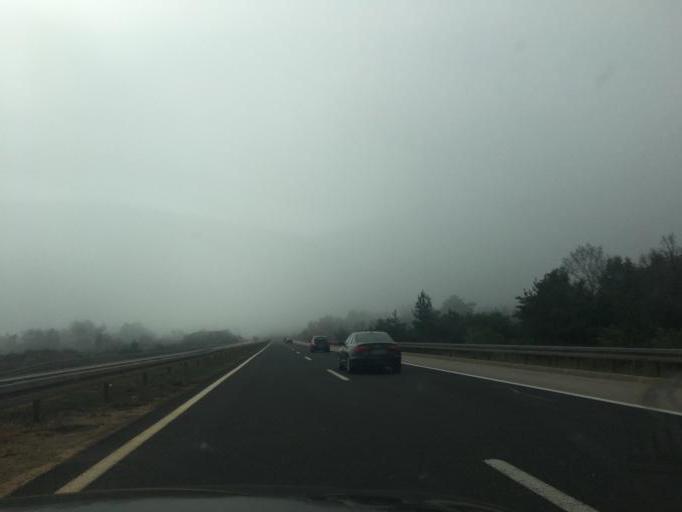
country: HR
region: Licko-Senjska
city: Gospic
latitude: 44.5473
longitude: 15.4347
